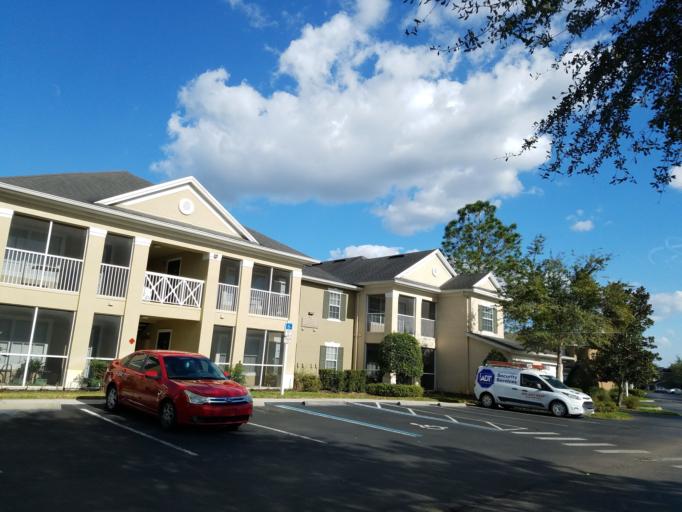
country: US
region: Florida
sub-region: Hillsborough County
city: Pebble Creek
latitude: 28.1895
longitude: -82.3695
